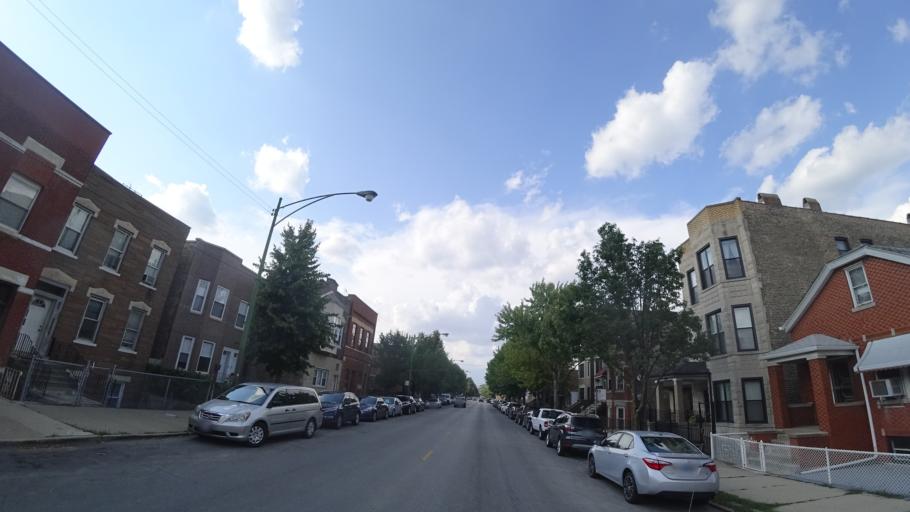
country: US
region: Illinois
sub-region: Cook County
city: Chicago
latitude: 41.8367
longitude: -87.6413
